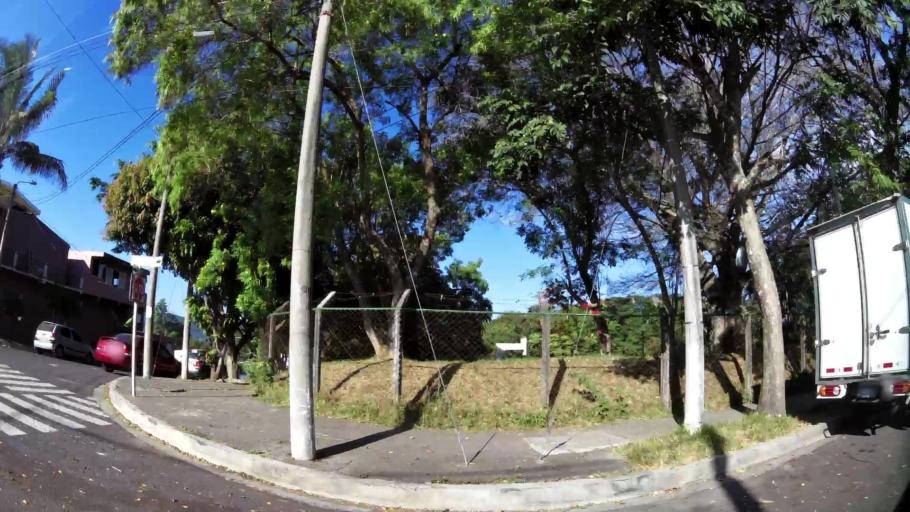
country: SV
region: La Libertad
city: Santa Tecla
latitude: 13.6827
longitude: -89.2899
